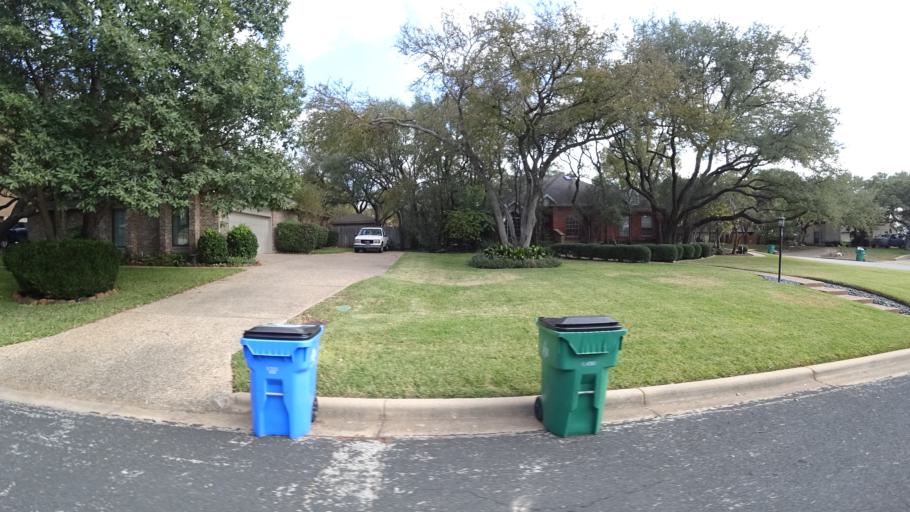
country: US
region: Texas
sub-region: Travis County
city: Shady Hollow
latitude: 30.1709
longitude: -97.8522
